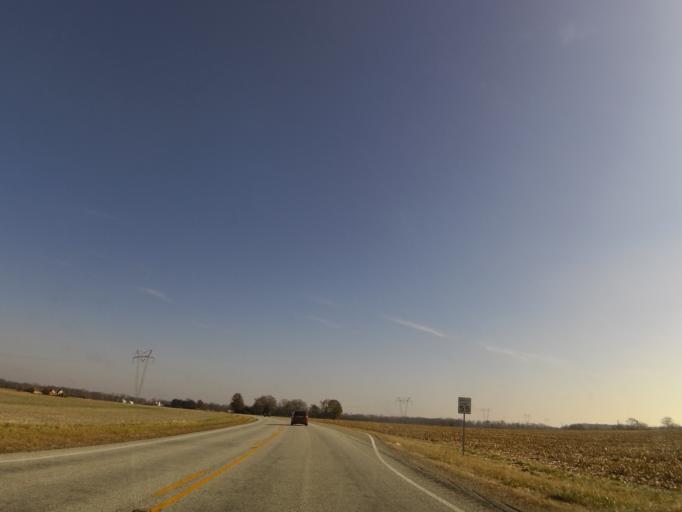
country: US
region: Indiana
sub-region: Shelby County
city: Morristown
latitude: 39.5729
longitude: -85.5963
